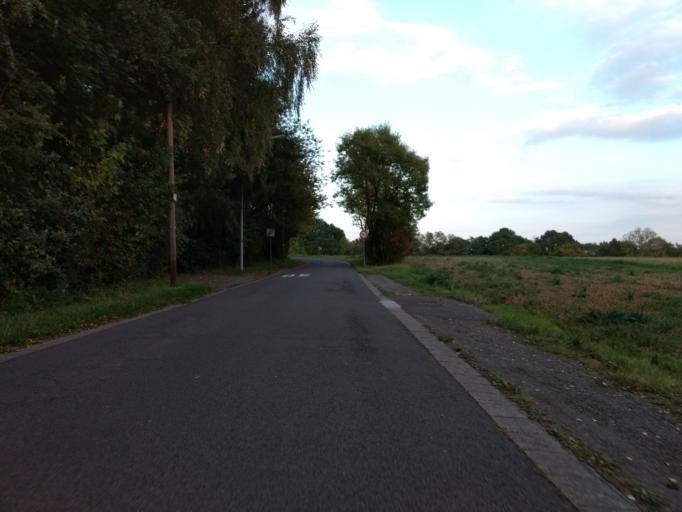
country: DE
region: Saarland
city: Nalbach
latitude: 49.3894
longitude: 6.7865
